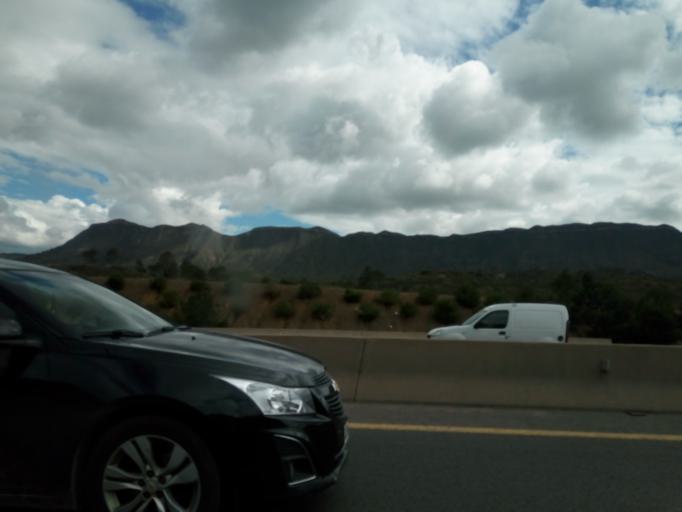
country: DZ
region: Bouira
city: Chorfa
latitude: 36.2456
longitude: 4.3070
